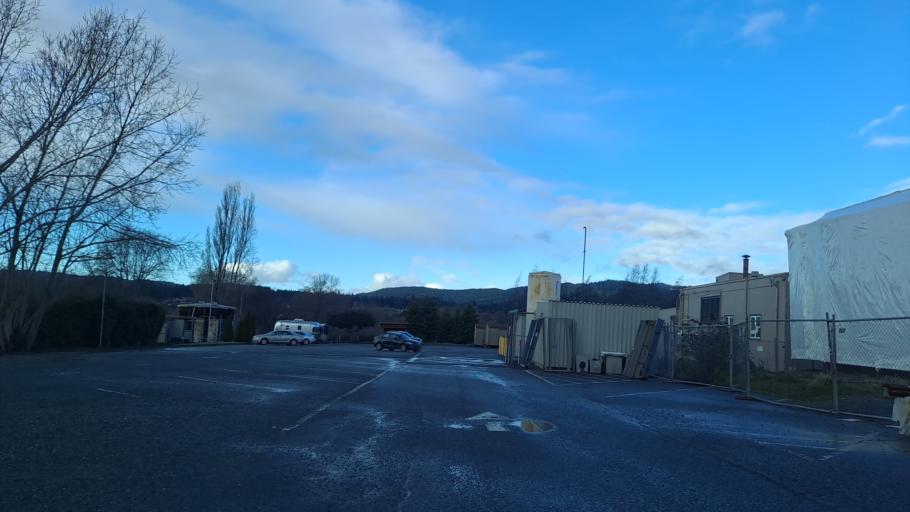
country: US
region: California
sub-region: Humboldt County
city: Fortuna
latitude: 40.5821
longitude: -124.1373
